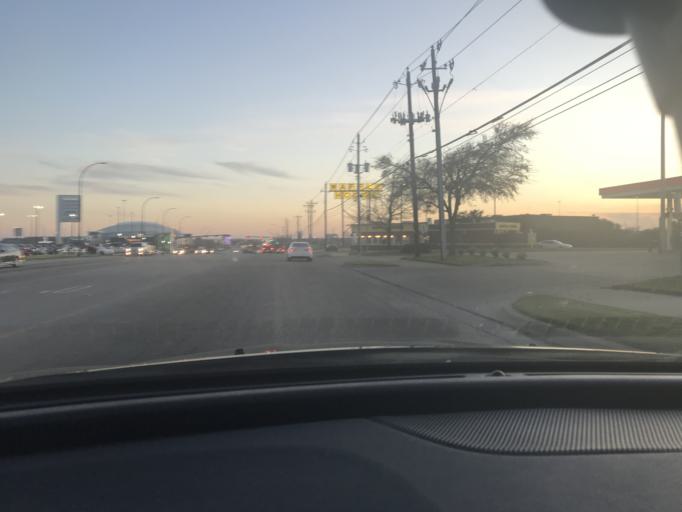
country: US
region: Texas
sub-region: Tarrant County
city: Arlington
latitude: 32.7655
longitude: -97.0972
